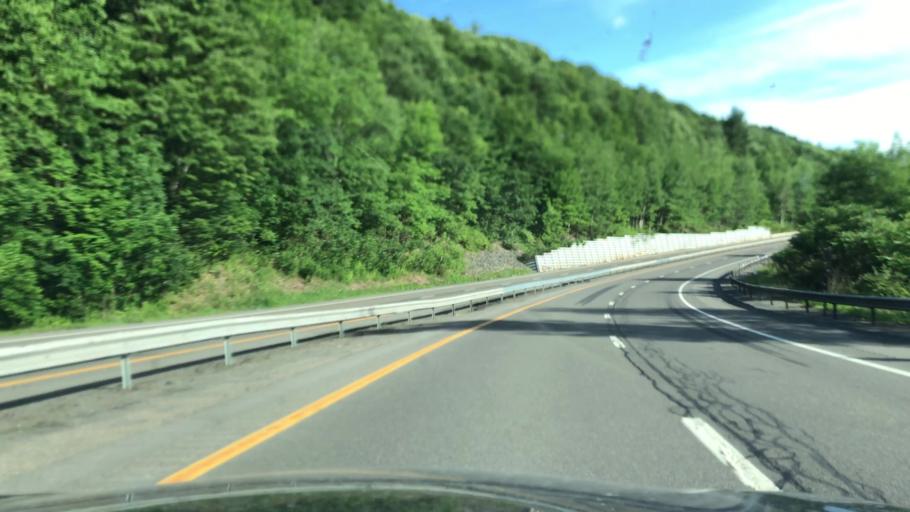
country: US
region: New York
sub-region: Delaware County
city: Hancock
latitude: 41.9876
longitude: -75.3364
